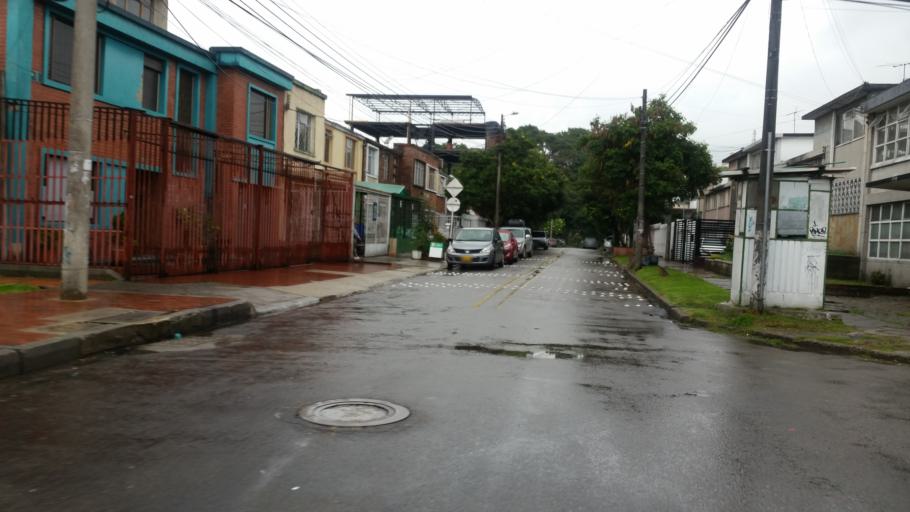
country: CO
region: Bogota D.C.
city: Barrio San Luis
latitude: 4.6610
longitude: -74.0698
